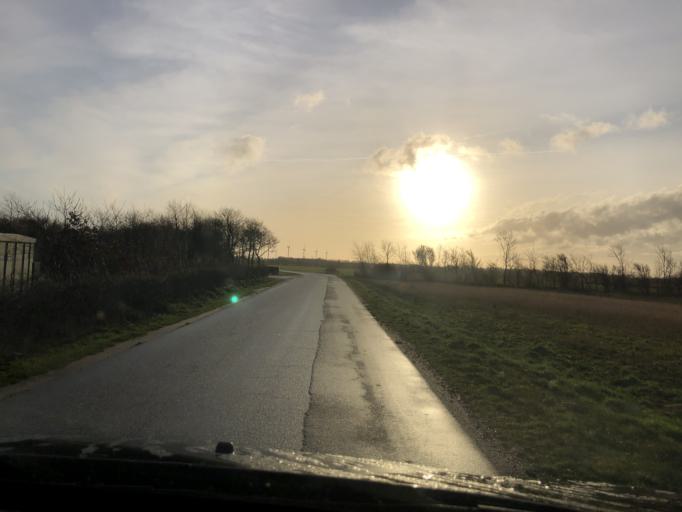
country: DK
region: Central Jutland
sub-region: Ringkobing-Skjern Kommune
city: Skjern
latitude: 55.8620
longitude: 8.3757
